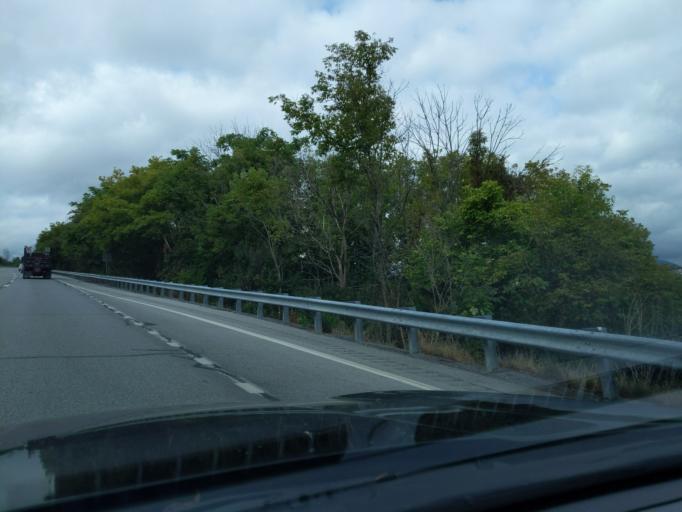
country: US
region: Pennsylvania
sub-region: Blair County
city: Hollidaysburg
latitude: 40.4193
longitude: -78.3947
